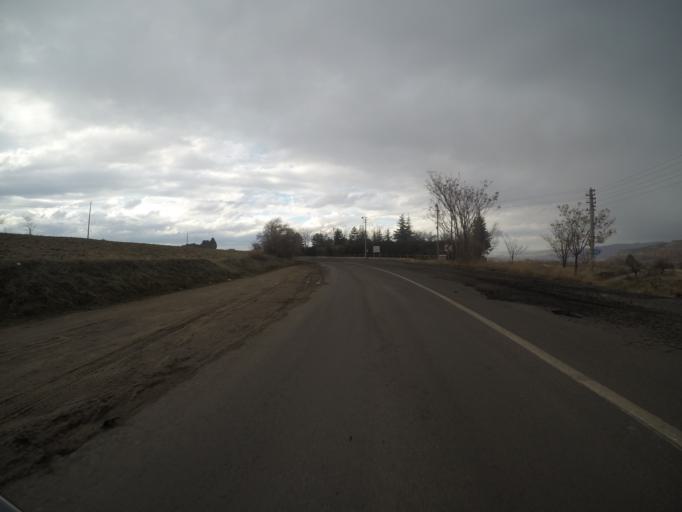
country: TR
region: Nevsehir
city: Goereme
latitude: 38.6364
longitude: 34.8553
